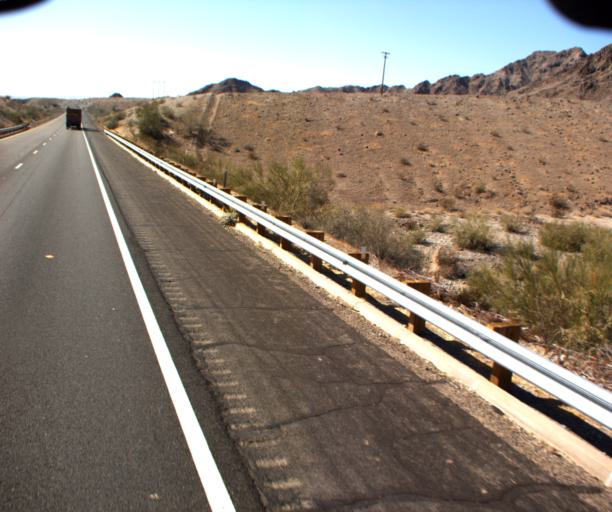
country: US
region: Arizona
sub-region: Yuma County
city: Fortuna Foothills
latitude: 32.6596
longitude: -114.3445
